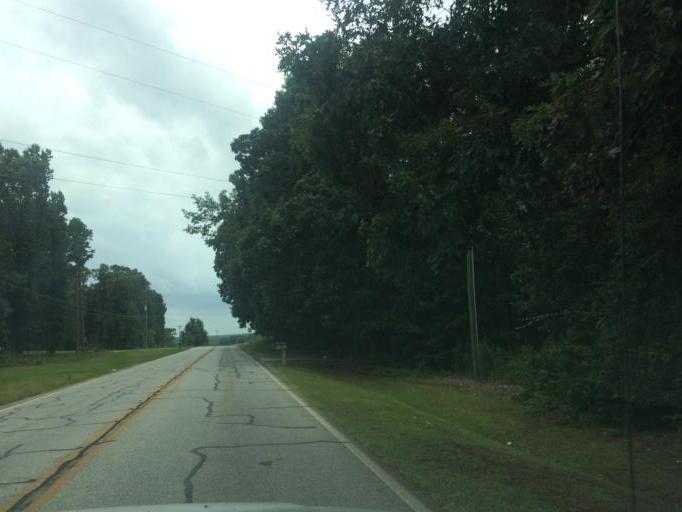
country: US
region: Georgia
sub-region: Hart County
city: Hartwell
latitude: 34.2628
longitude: -82.8959
